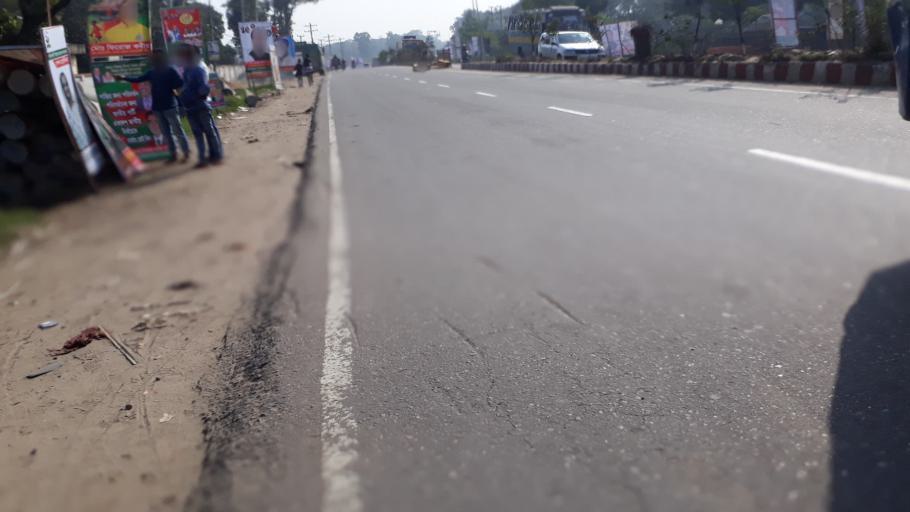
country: BD
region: Dhaka
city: Tungi
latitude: 23.8950
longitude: 90.2713
